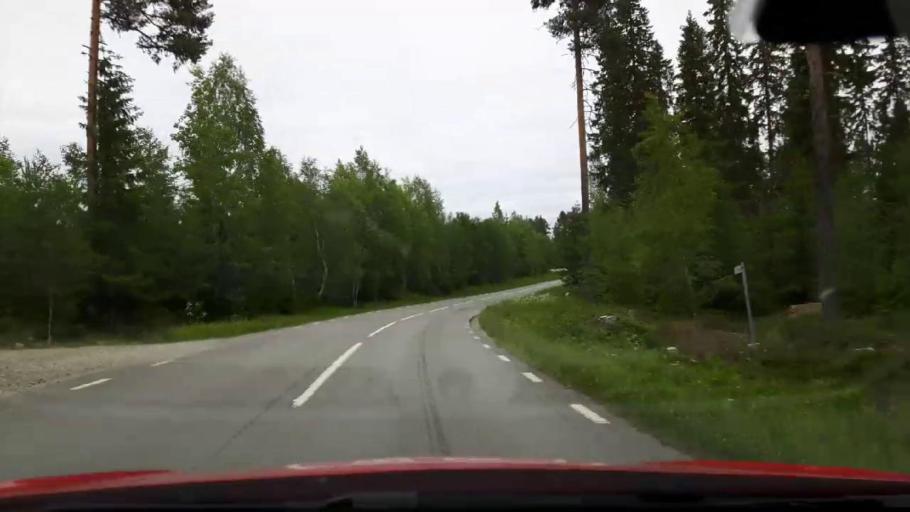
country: SE
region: Jaemtland
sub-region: Stroemsunds Kommun
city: Stroemsund
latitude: 63.4196
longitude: 15.5486
